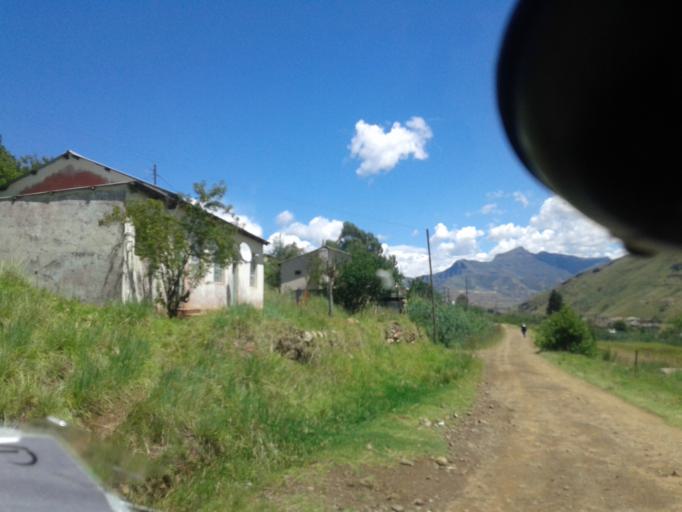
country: LS
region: Qacha's Nek
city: Qacha's Nek
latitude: -30.0941
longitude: 28.6450
